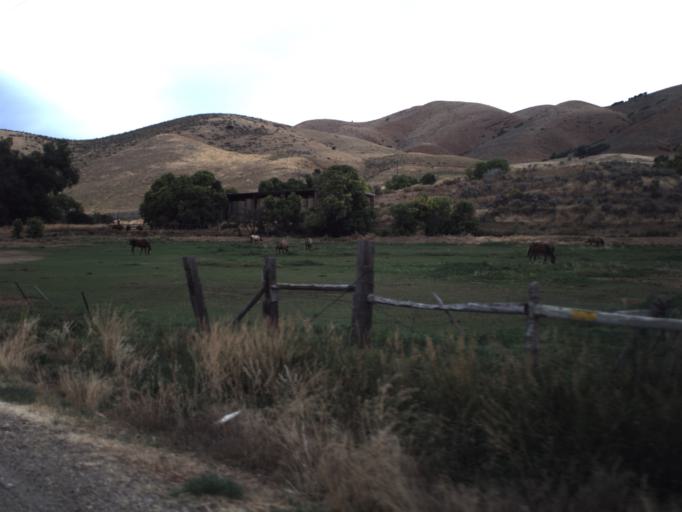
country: US
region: Utah
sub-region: Morgan County
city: Morgan
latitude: 41.0166
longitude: -111.6766
